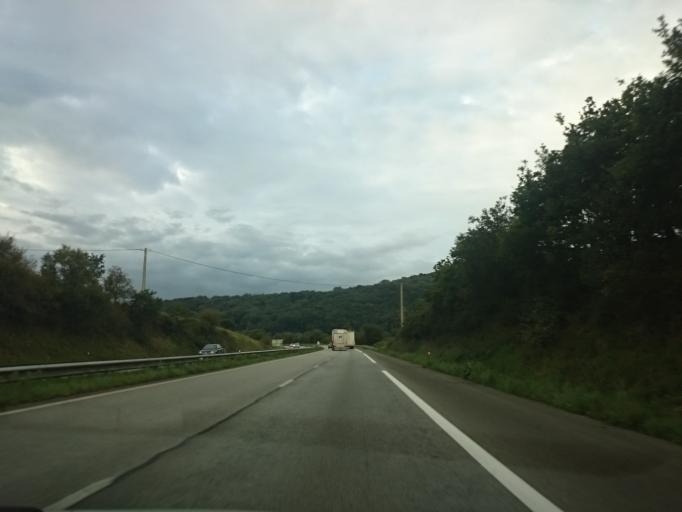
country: FR
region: Brittany
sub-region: Departement du Finistere
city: Chateaulin
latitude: 48.1879
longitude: -4.0466
